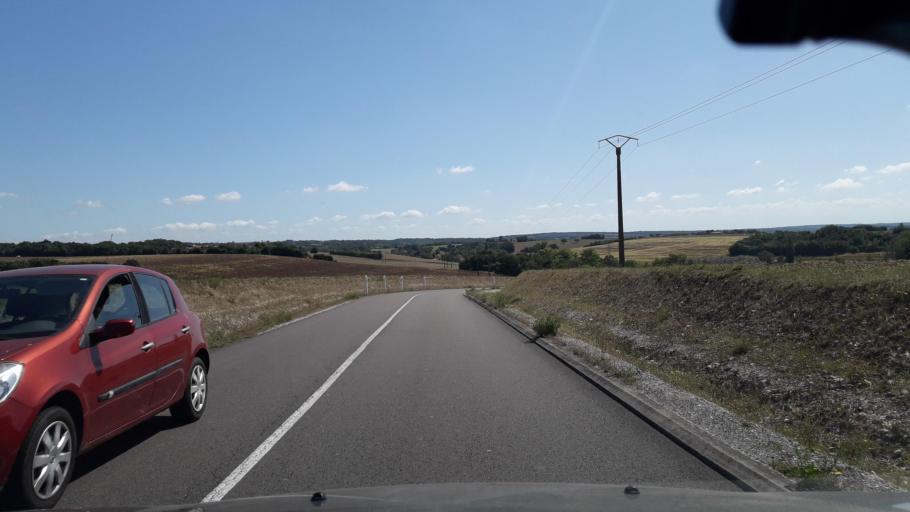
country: FR
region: Poitou-Charentes
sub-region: Departement de la Charente
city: Champniers
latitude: 45.6941
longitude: 0.1925
